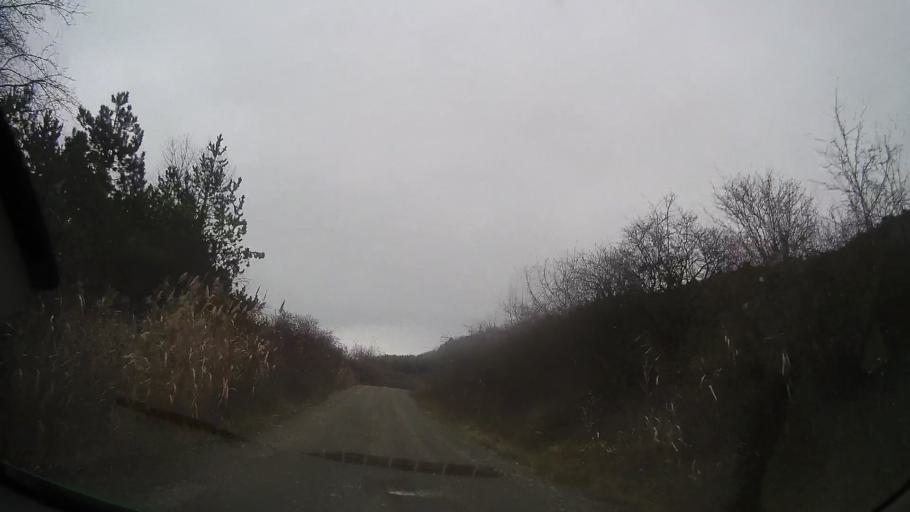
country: RO
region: Mures
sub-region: Comuna Bala
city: Bala
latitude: 46.6815
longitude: 24.4869
